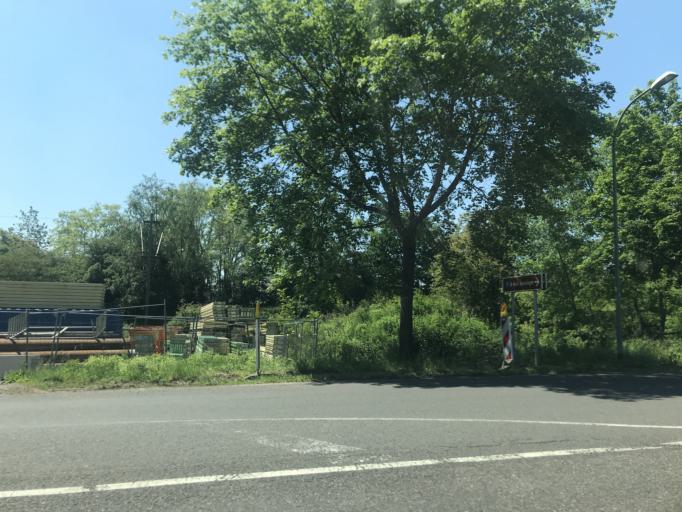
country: DE
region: Saarland
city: Merzig
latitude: 49.4657
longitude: 6.6183
